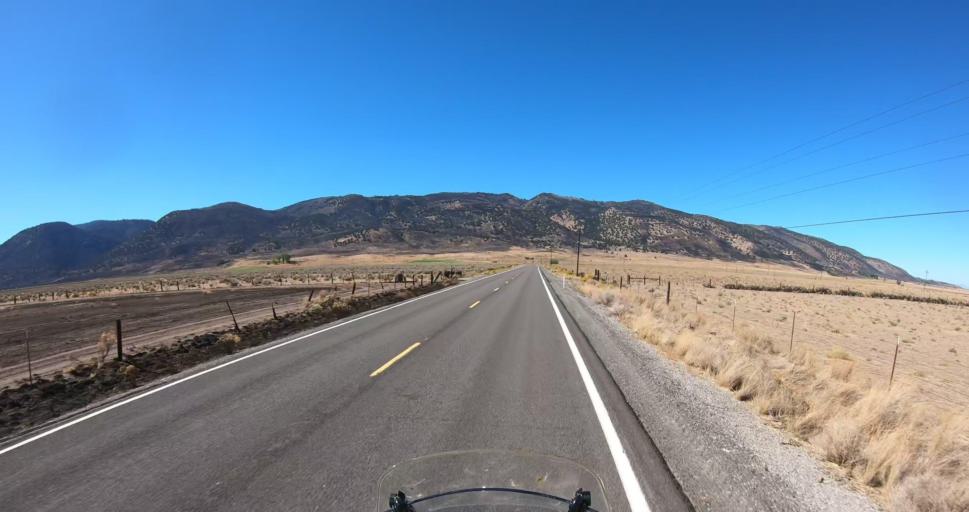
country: US
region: Oregon
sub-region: Lake County
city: Lakeview
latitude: 42.6172
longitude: -120.4918
